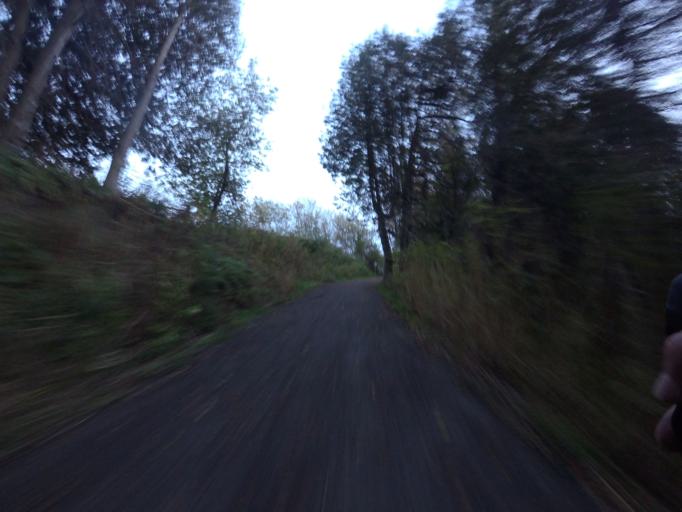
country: CA
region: Ontario
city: Oshawa
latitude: 43.9017
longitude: -78.5996
